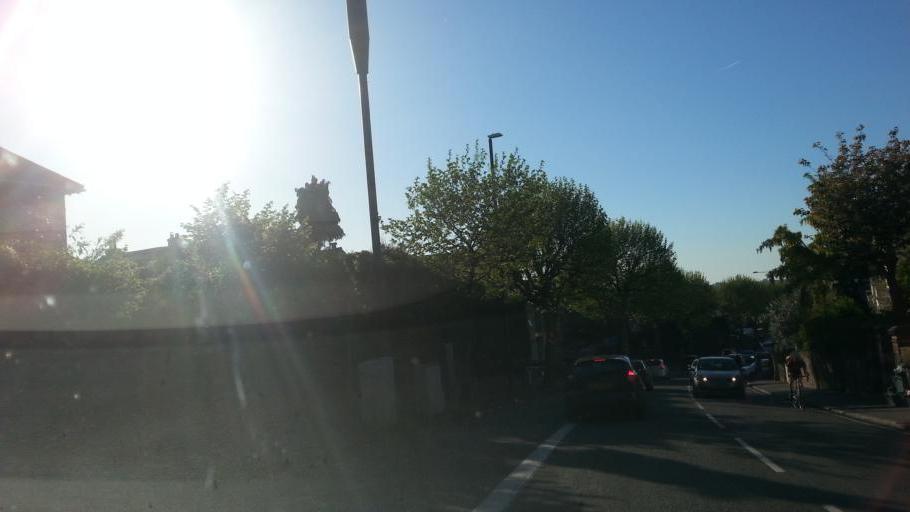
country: GB
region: England
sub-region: Bristol
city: Bristol
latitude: 51.4382
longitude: -2.5717
